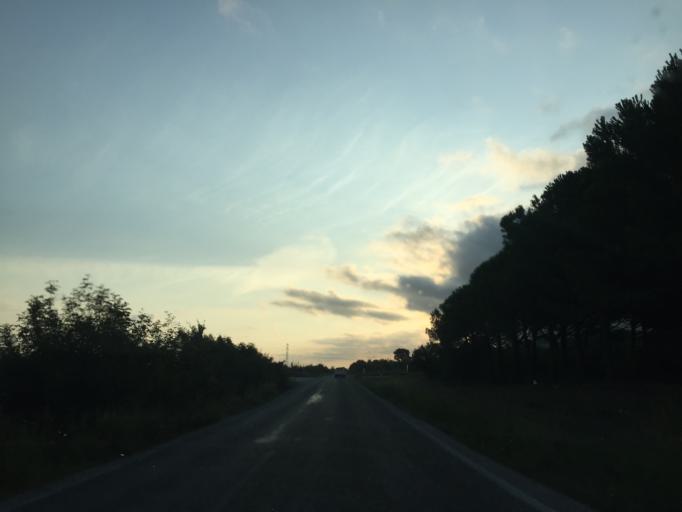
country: TR
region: Balikesir
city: Tutuncu
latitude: 40.1069
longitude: 27.7000
